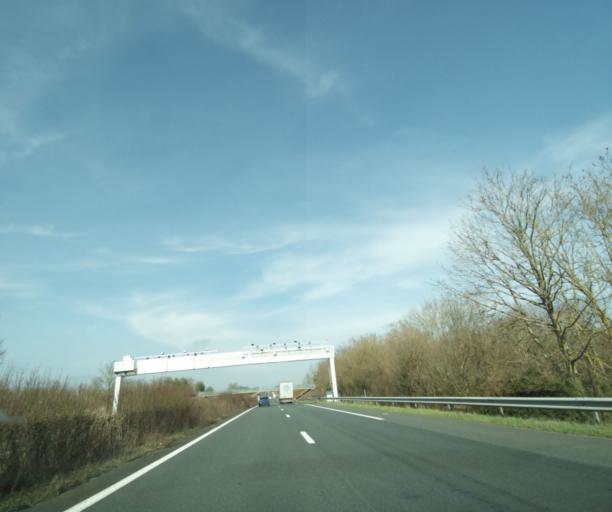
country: FR
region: Centre
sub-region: Departement de l'Indre
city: Vatan
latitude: 46.9773
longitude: 1.7670
